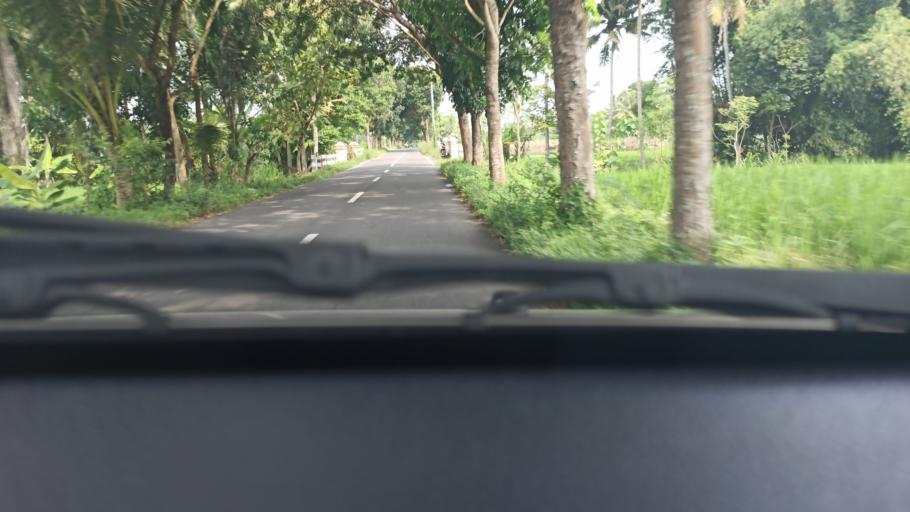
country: ID
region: Daerah Istimewa Yogyakarta
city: Sleman
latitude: -7.6953
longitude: 110.2986
